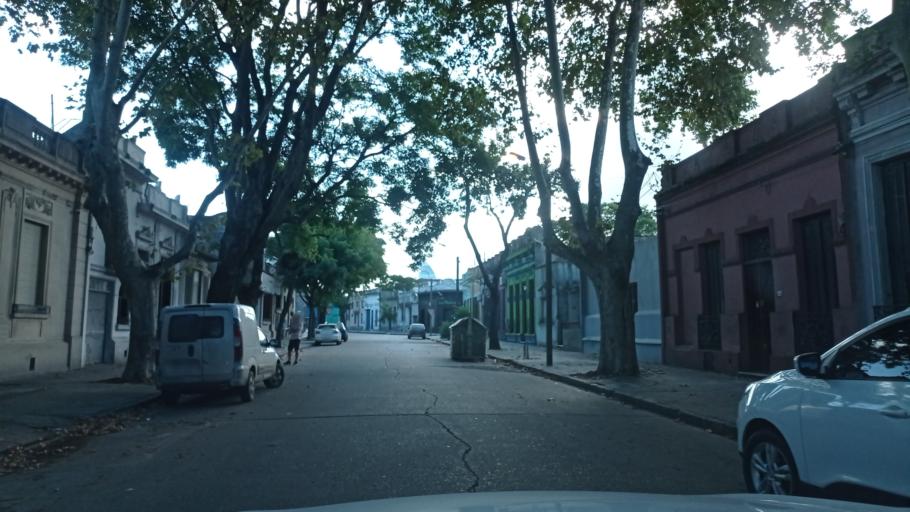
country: UY
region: Montevideo
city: Montevideo
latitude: -34.8919
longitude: -56.1803
